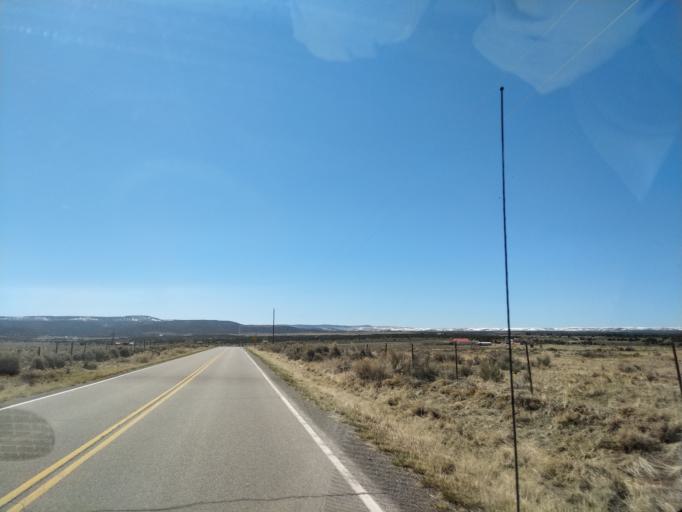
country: US
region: Colorado
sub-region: Mesa County
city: Redlands
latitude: 38.9925
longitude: -108.7509
